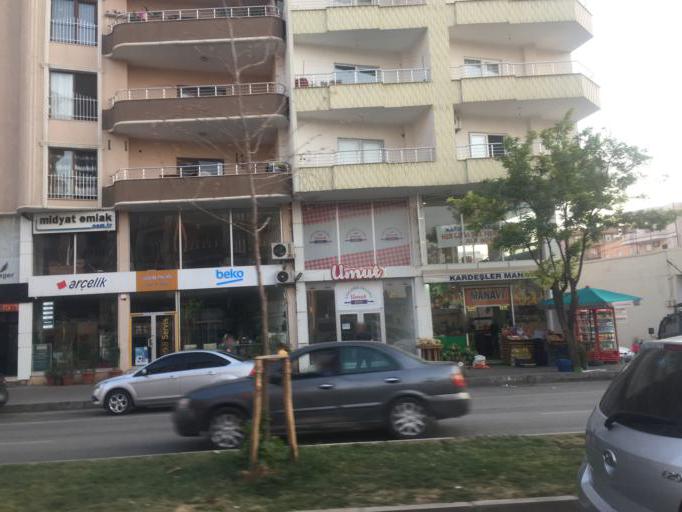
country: TR
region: Mardin
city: Midyat
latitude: 37.4232
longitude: 41.3450
